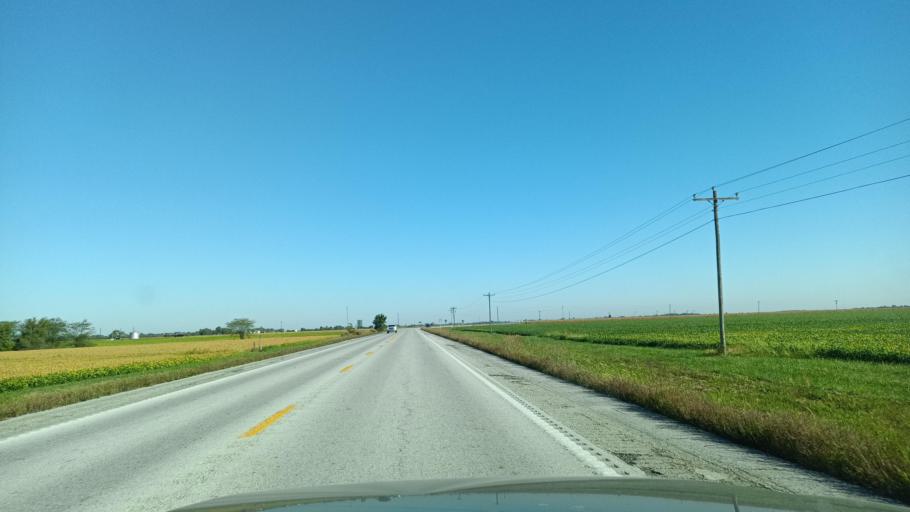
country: US
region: Missouri
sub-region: Audrain County
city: Vandalia
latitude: 39.4069
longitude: -91.6415
